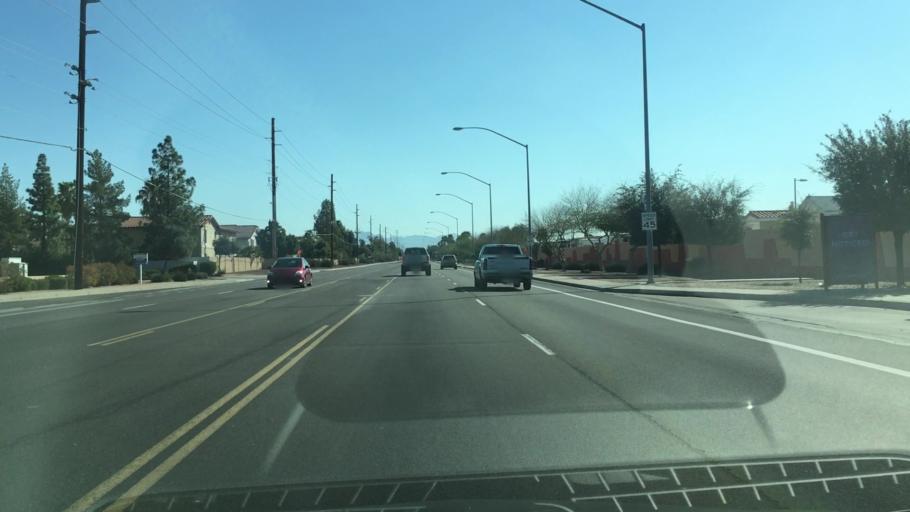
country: US
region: Arizona
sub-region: Maricopa County
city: Mesa
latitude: 33.4234
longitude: -111.7705
